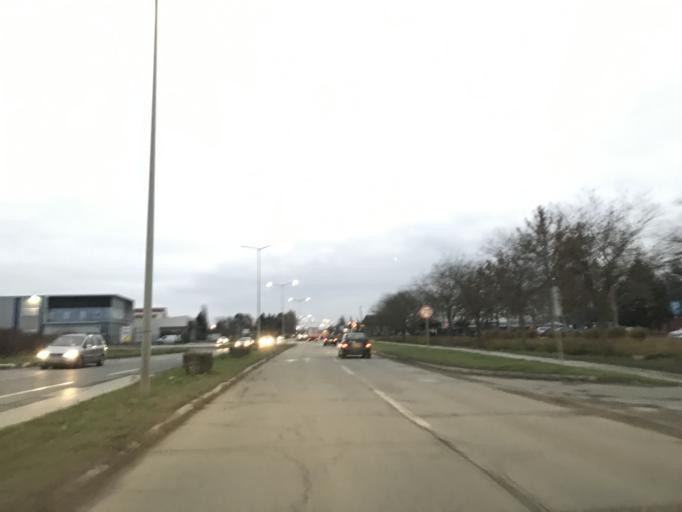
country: RS
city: Veternik
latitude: 45.2783
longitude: 19.7947
